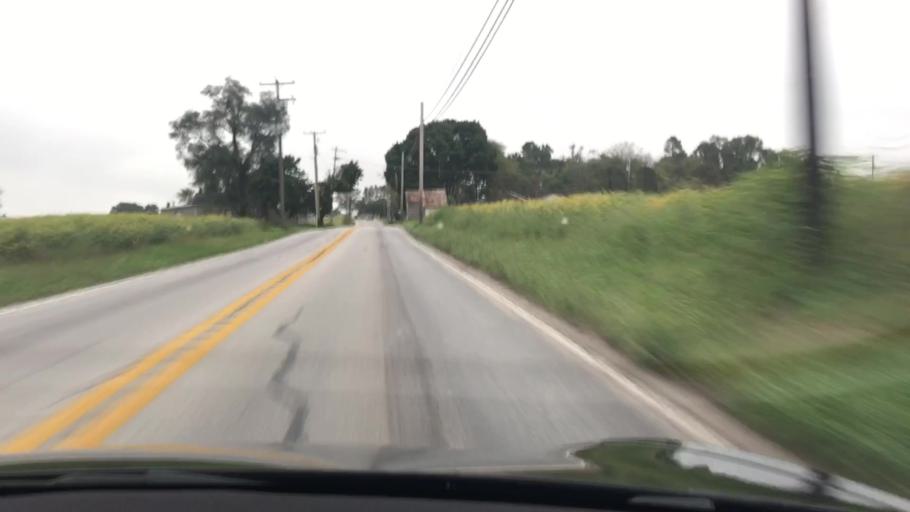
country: US
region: Pennsylvania
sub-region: York County
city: Weigelstown
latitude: 40.0096
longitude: -76.8254
